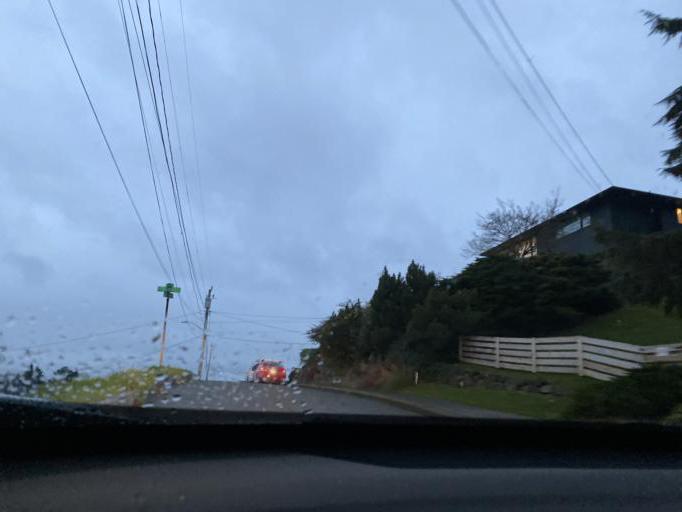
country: US
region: Washington
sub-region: King County
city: Seattle
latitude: 47.6459
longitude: -122.3890
